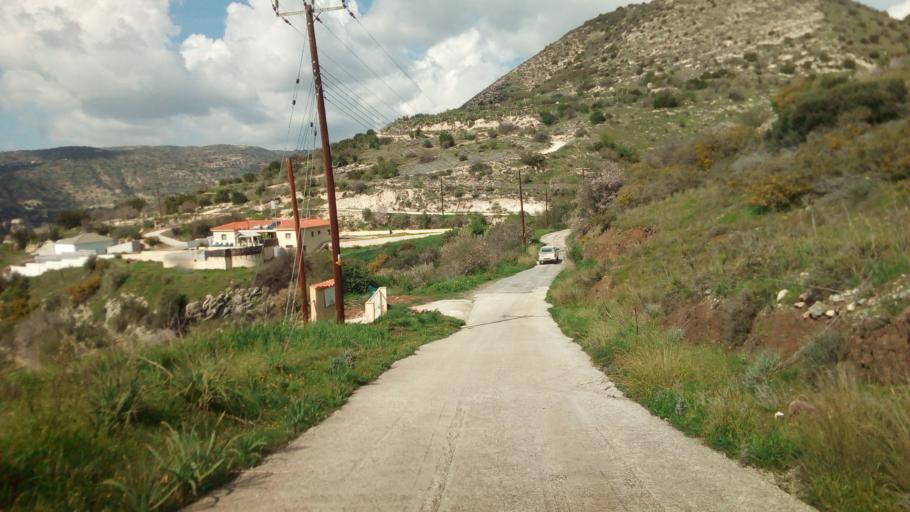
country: CY
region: Pafos
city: Mesogi
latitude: 34.7890
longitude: 32.5424
